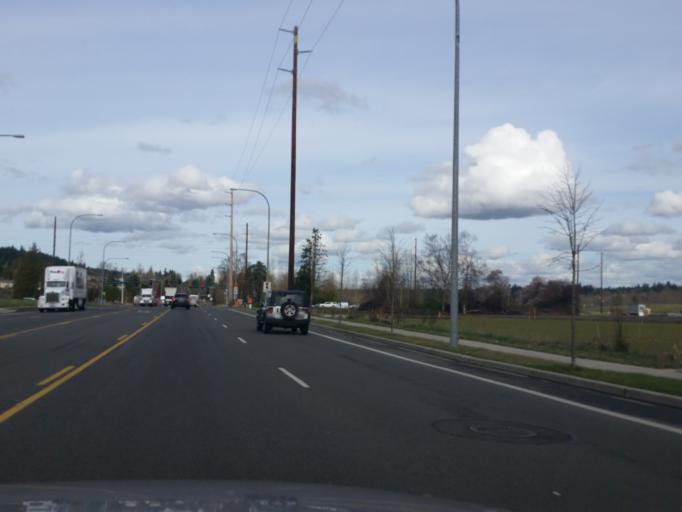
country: US
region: Washington
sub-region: Pierce County
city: Fife
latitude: 47.2370
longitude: -122.3363
